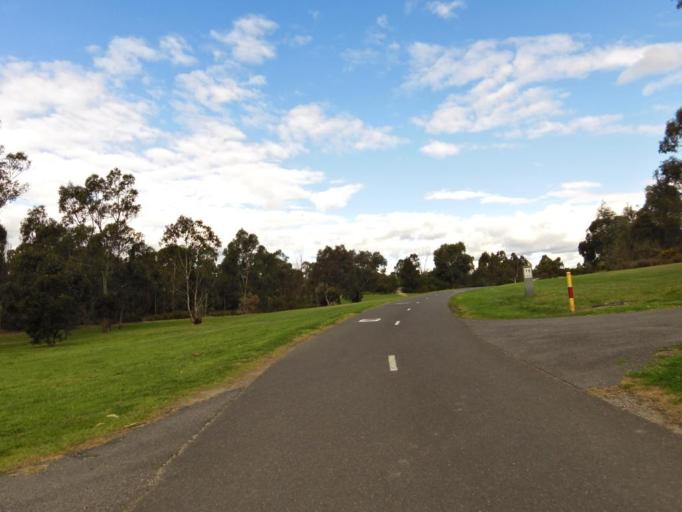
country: AU
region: Victoria
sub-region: Boroondara
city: Balwyn North
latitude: -37.7825
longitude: 145.0975
